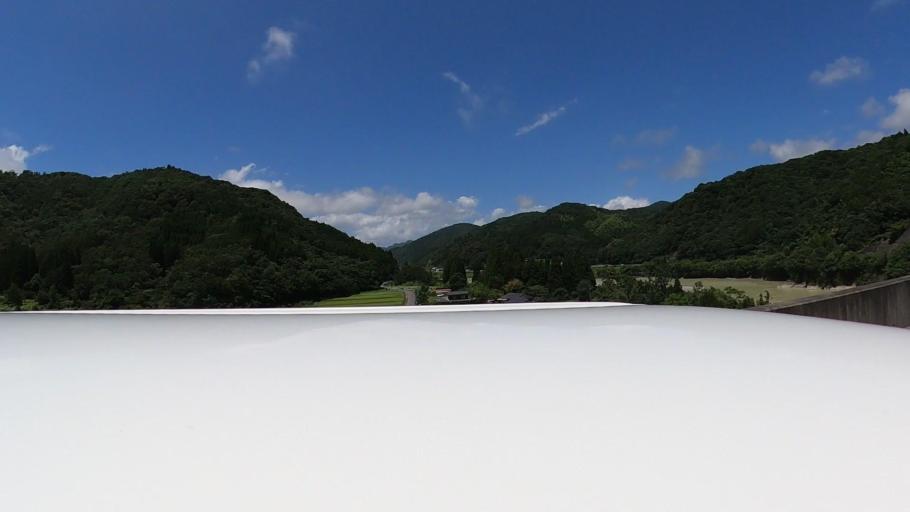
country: JP
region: Miyazaki
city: Takanabe
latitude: 32.3426
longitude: 131.5982
